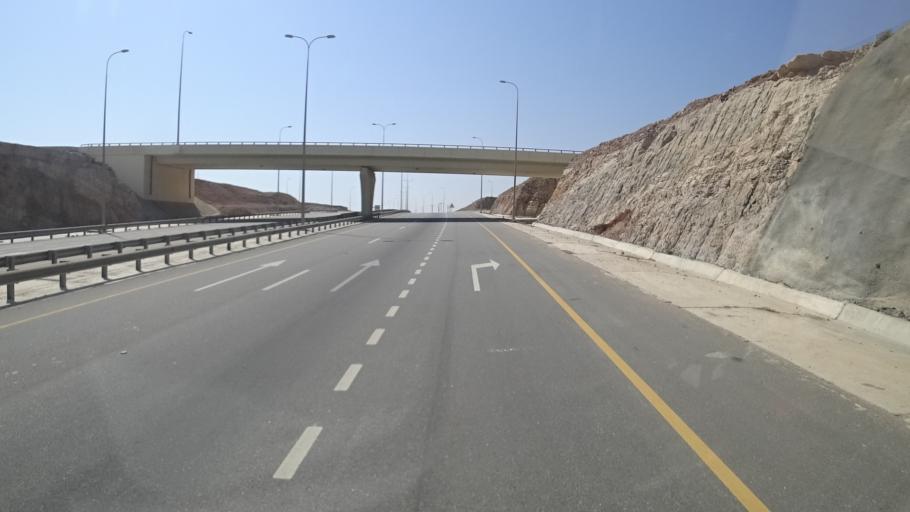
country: OM
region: Zufar
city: Salalah
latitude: 17.0308
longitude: 54.6126
